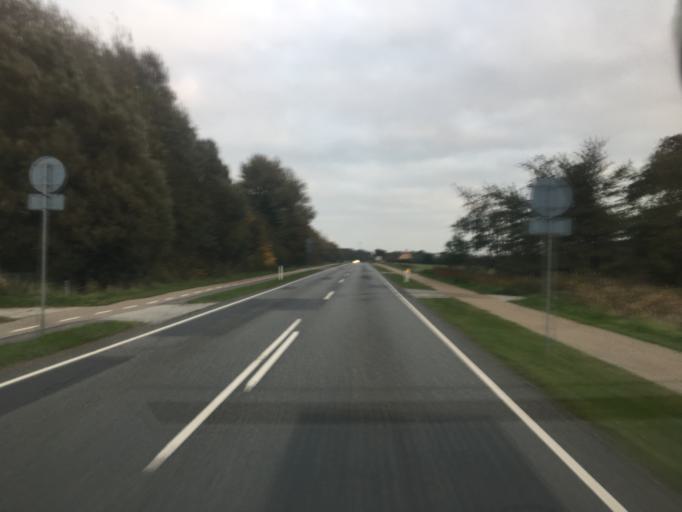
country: DK
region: South Denmark
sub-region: Tonder Kommune
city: Tonder
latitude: 54.9471
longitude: 8.8374
